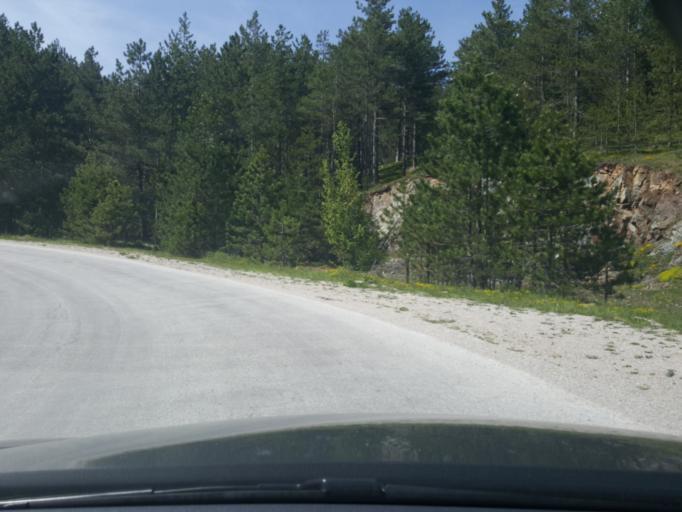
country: RS
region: Central Serbia
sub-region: Zlatiborski Okrug
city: Bajina Basta
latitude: 43.8784
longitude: 19.5662
